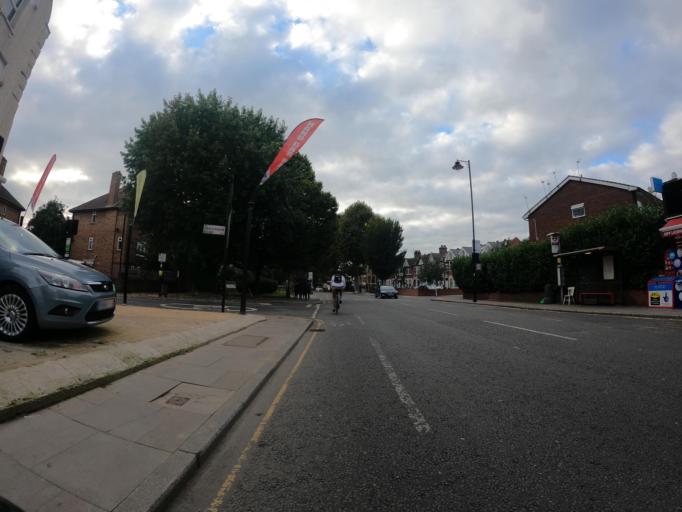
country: GB
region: England
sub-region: Greater London
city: Ealing
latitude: 51.5096
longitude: -0.3290
